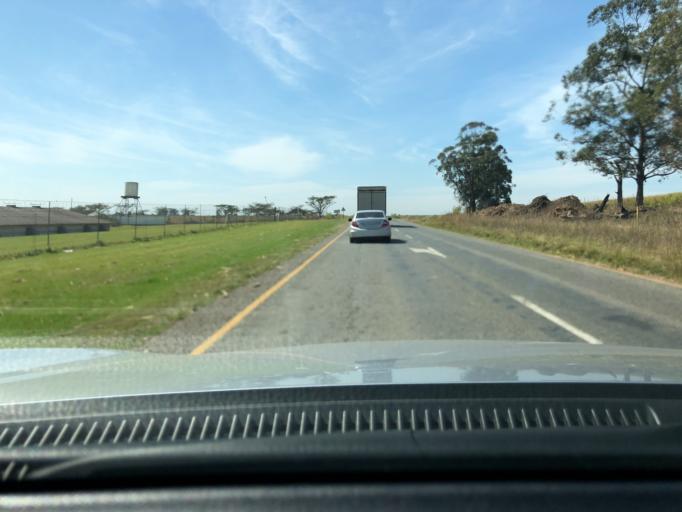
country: ZA
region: KwaZulu-Natal
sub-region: uMgungundlovu District Municipality
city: Camperdown
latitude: -29.7311
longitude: 30.4528
